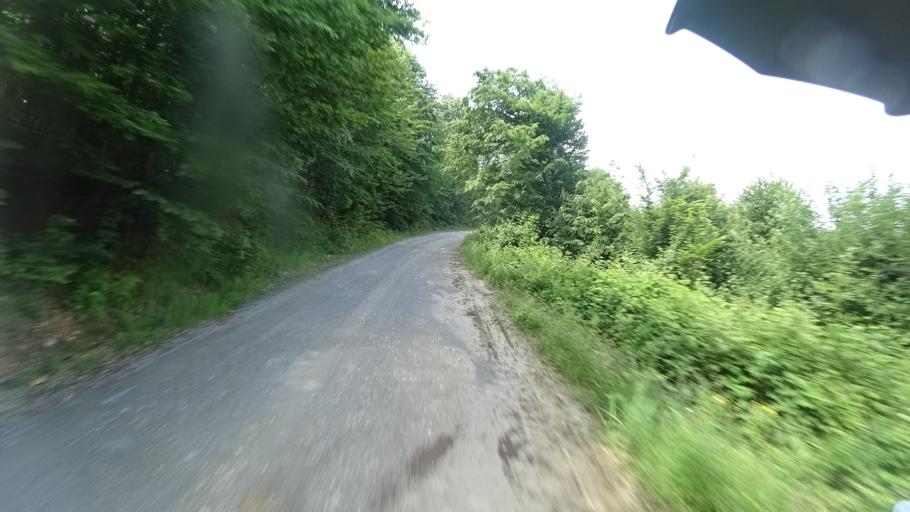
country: HR
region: Sisacko-Moslavacka
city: Gvozd
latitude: 45.3277
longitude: 15.8390
